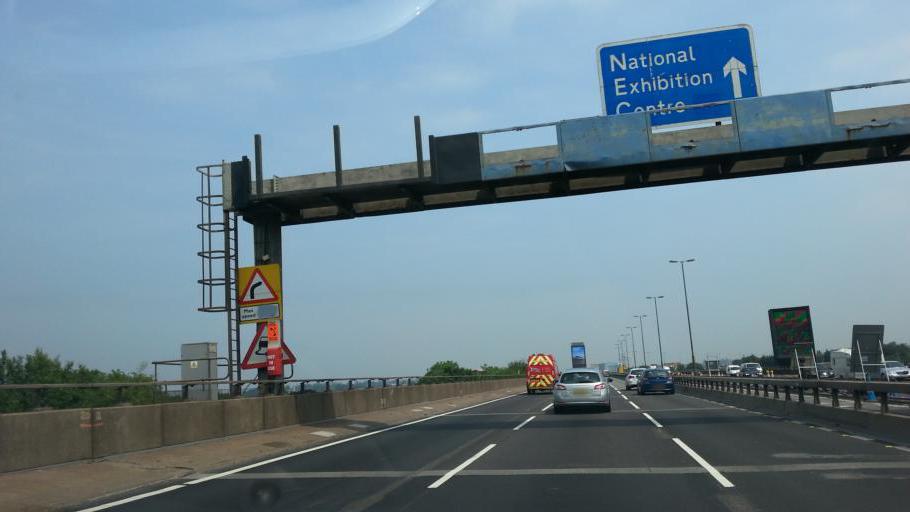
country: GB
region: England
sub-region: Sandwell
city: Oldbury
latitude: 52.4994
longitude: -2.0123
